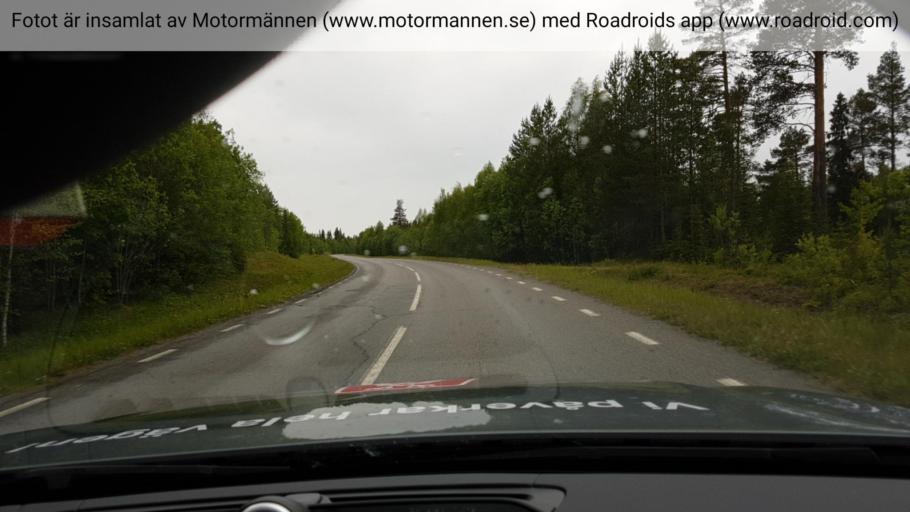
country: SE
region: Jaemtland
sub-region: Stroemsunds Kommun
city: Stroemsund
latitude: 63.5962
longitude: 15.3317
